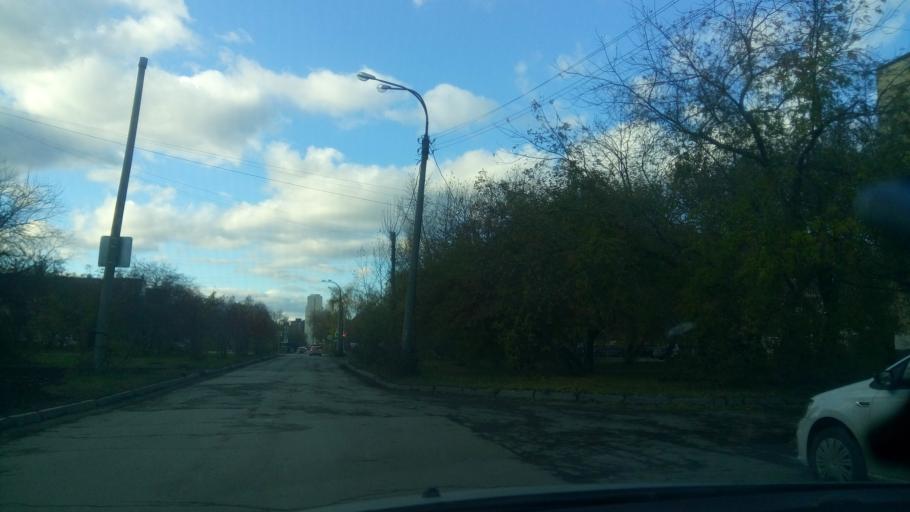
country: RU
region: Sverdlovsk
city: Yekaterinburg
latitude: 56.8670
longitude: 60.5382
